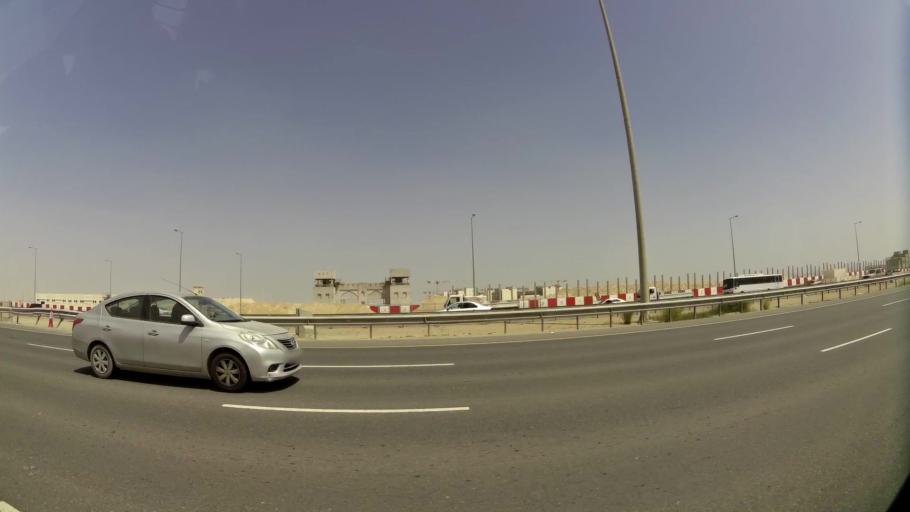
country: QA
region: Baladiyat ar Rayyan
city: Ar Rayyan
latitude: 25.3594
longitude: 51.4505
